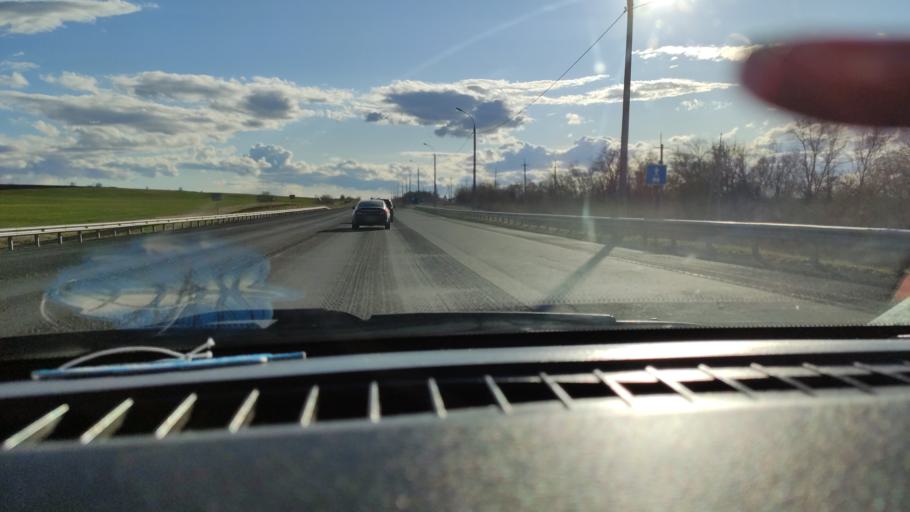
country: RU
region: Saratov
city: Shumeyka
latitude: 51.7878
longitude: 46.1431
